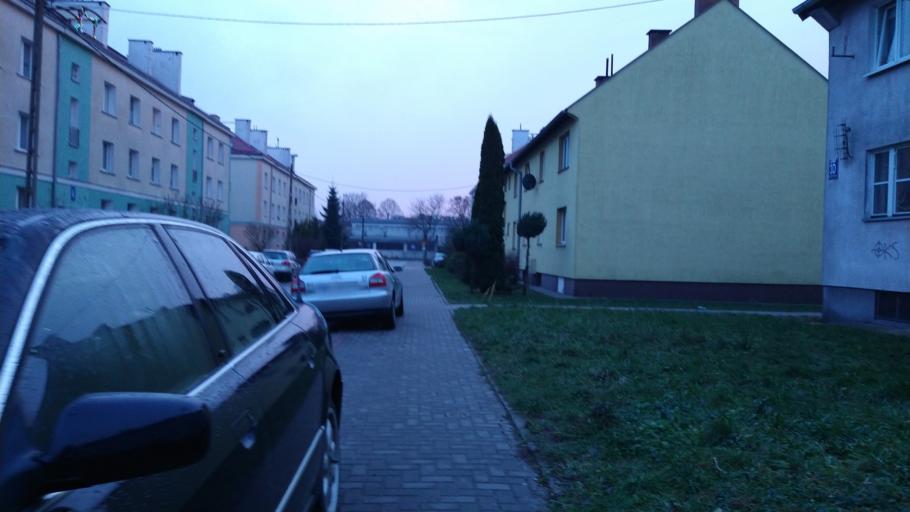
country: PL
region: Warmian-Masurian Voivodeship
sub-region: Powiat olsztynski
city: Olsztyn
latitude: 53.7883
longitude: 20.4962
